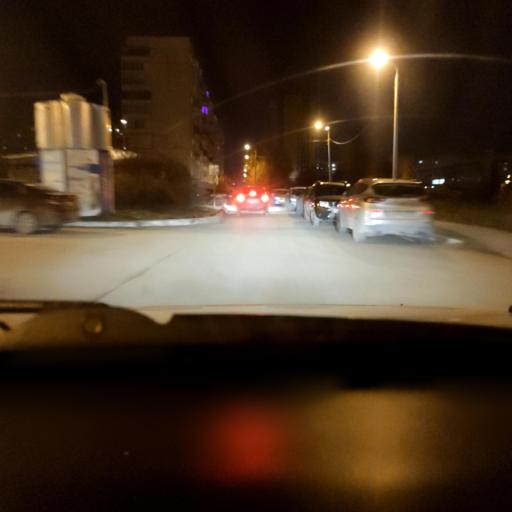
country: RU
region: Perm
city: Perm
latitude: 57.9746
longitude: 56.2027
